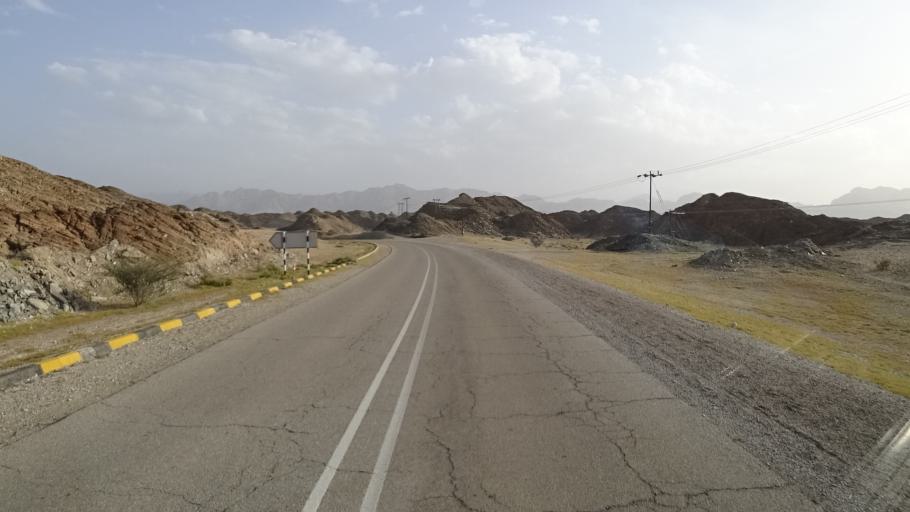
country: OM
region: Muhafazat Masqat
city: Bawshar
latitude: 23.3643
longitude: 58.5249
